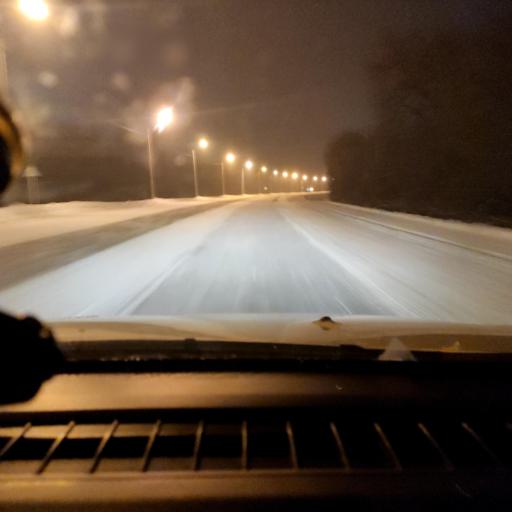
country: RU
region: Samara
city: Georgiyevka
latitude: 53.2677
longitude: 51.0114
